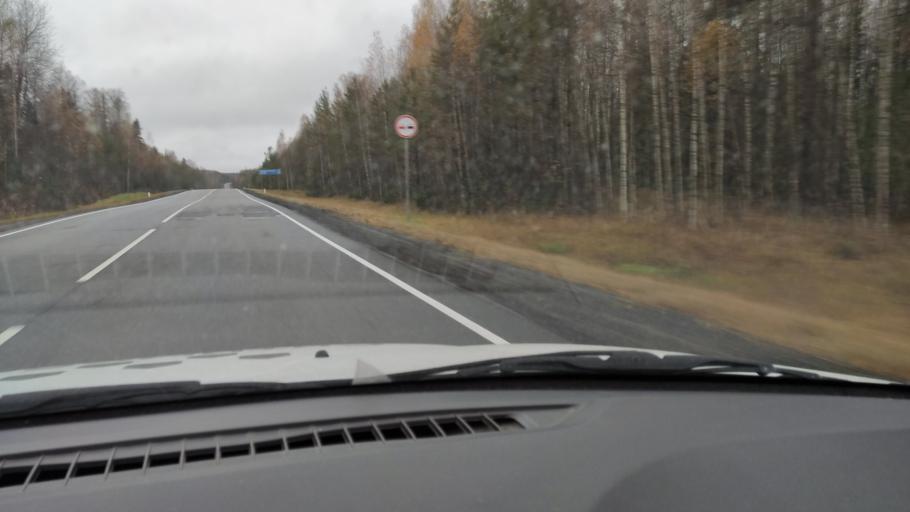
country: RU
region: Kirov
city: Chernaya Kholunitsa
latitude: 58.8626
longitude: 51.5989
